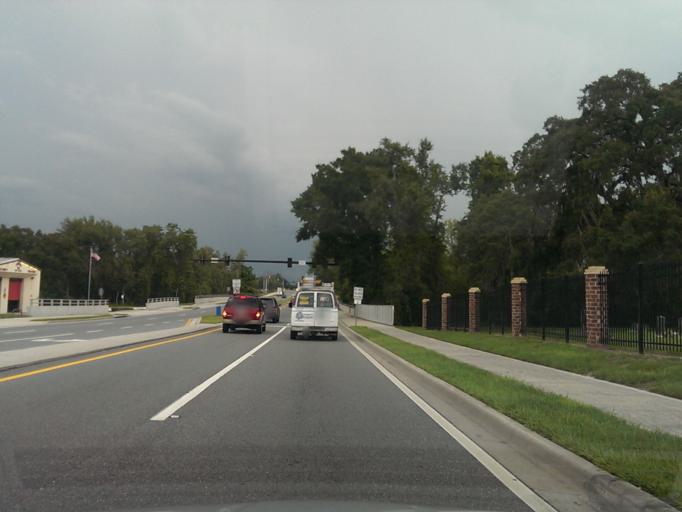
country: US
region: Florida
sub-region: Orange County
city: Lake Butler
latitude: 28.4995
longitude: -81.5870
